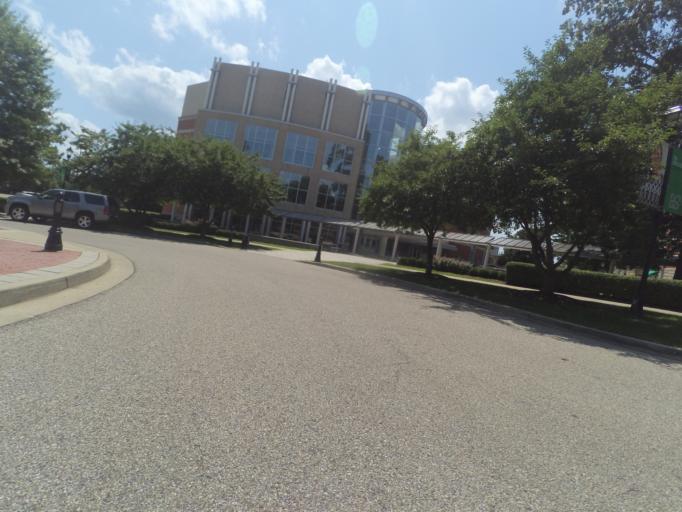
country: US
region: West Virginia
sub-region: Cabell County
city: Huntington
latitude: 38.4229
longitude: -82.4301
